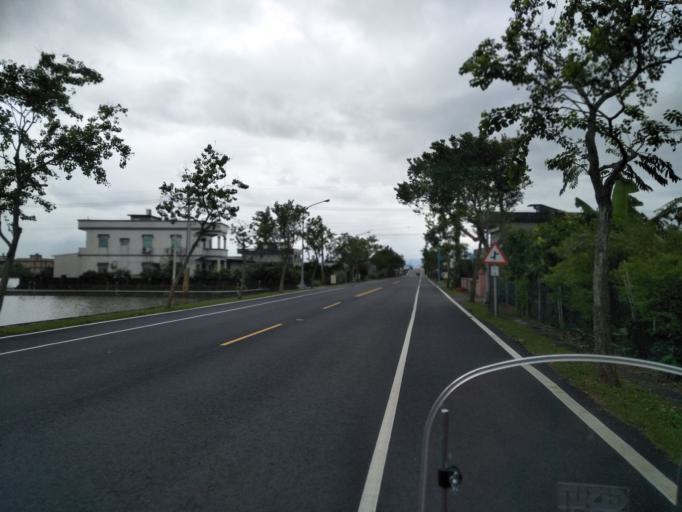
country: TW
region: Taiwan
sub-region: Yilan
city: Yilan
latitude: 24.8130
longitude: 121.7933
